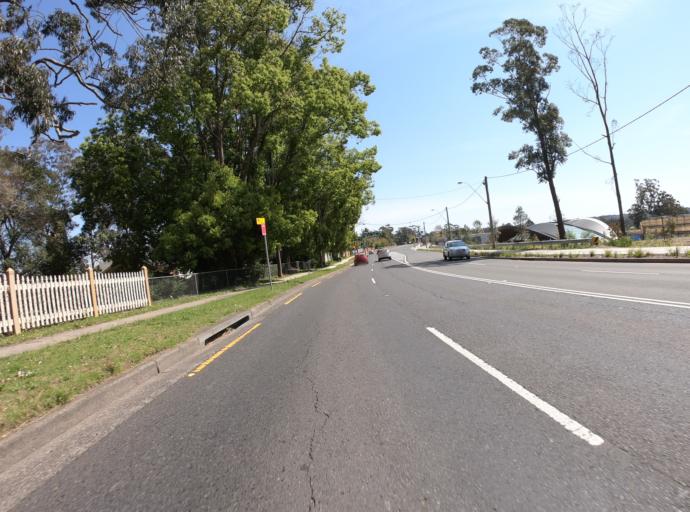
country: AU
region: New South Wales
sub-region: The Hills Shire
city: West Pennant
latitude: -33.7378
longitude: 151.0324
